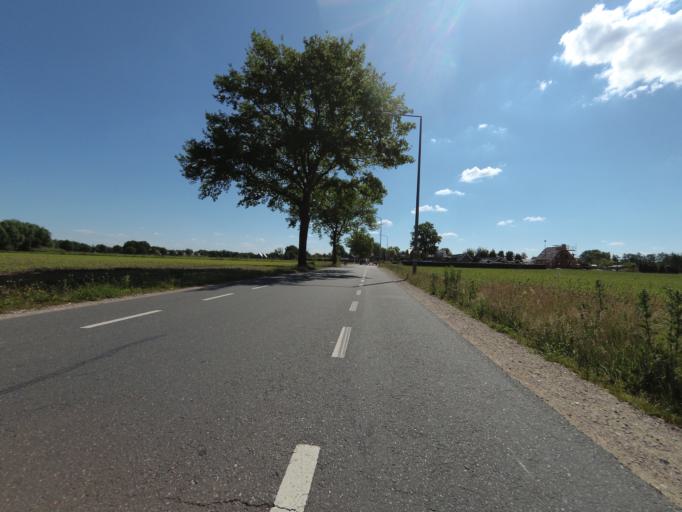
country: NL
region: Gelderland
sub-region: Gemeente Barneveld
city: Kootwijkerbroek
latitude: 52.1196
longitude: 5.6793
